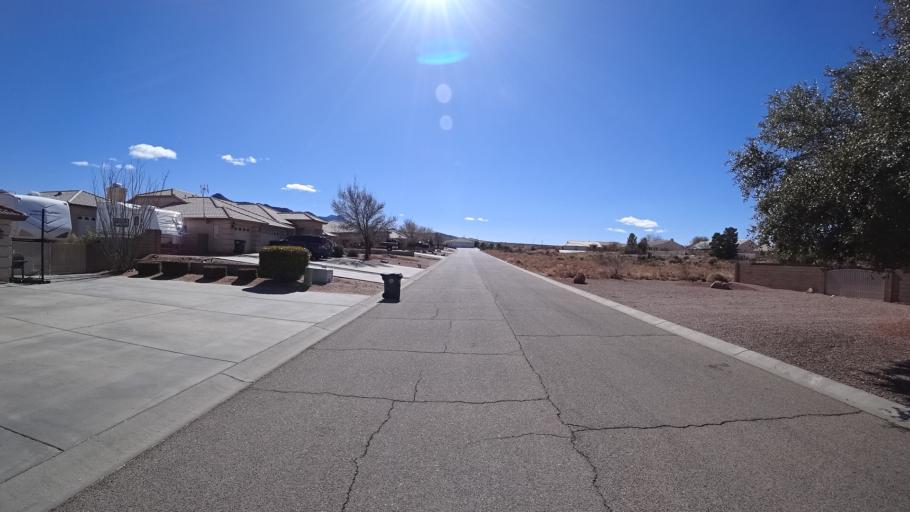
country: US
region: Arizona
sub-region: Mohave County
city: Kingman
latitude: 35.1992
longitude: -113.9593
